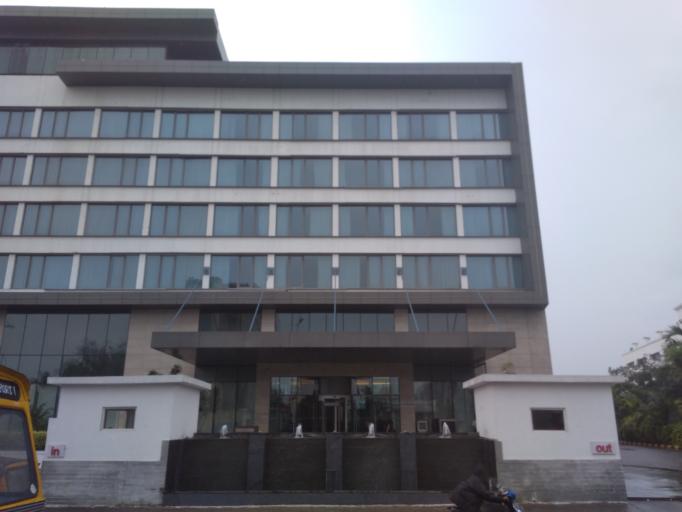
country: IN
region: Tamil Nadu
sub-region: Kancheepuram
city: Injambakkam
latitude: 12.9056
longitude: 80.2279
